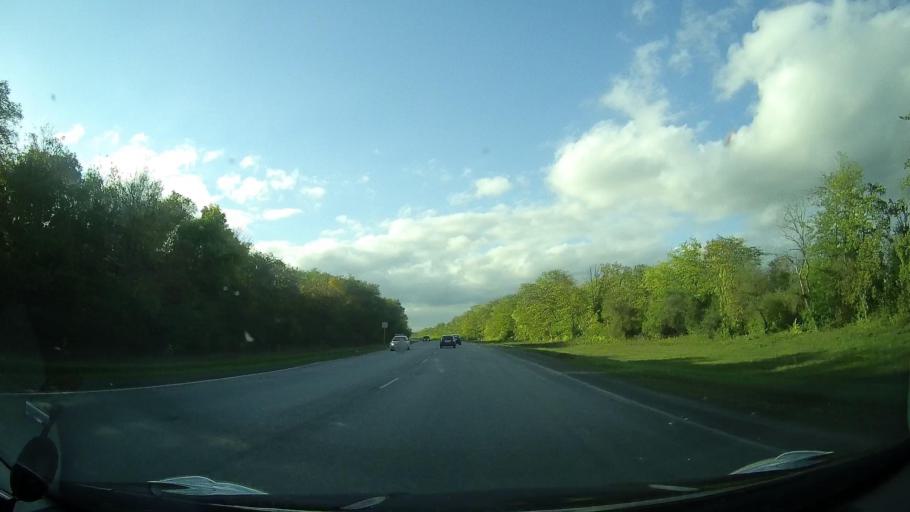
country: RU
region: Rostov
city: Kirovskaya
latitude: 46.9906
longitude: 40.0217
